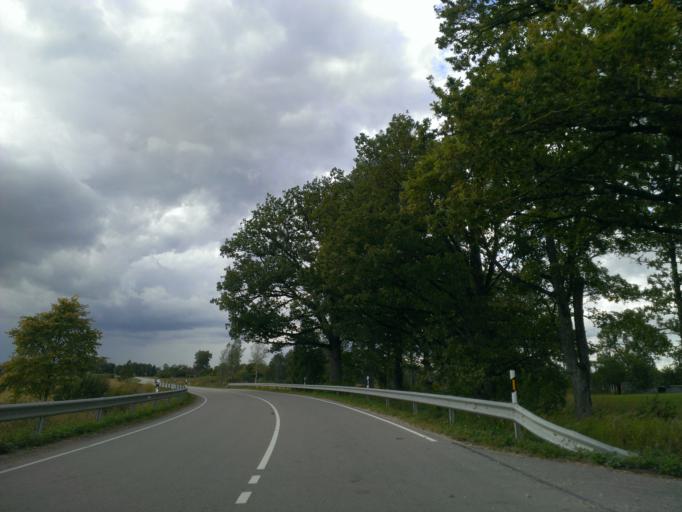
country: LV
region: Malpils
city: Malpils
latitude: 56.8945
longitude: 25.1537
